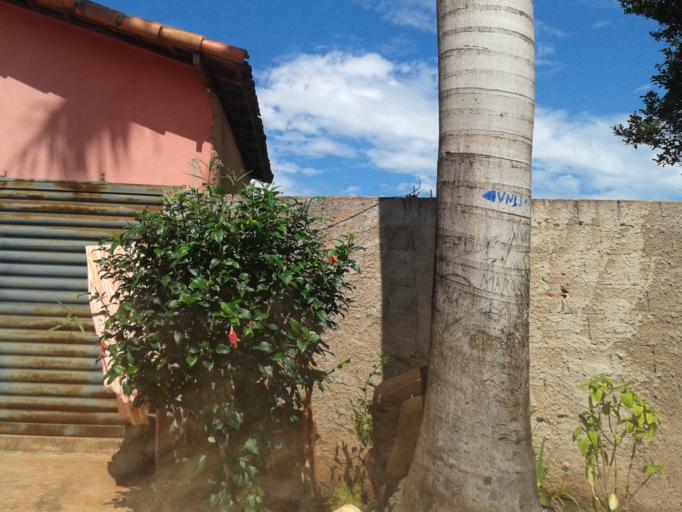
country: BR
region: Minas Gerais
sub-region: Capinopolis
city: Capinopolis
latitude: -18.5157
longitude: -49.5037
